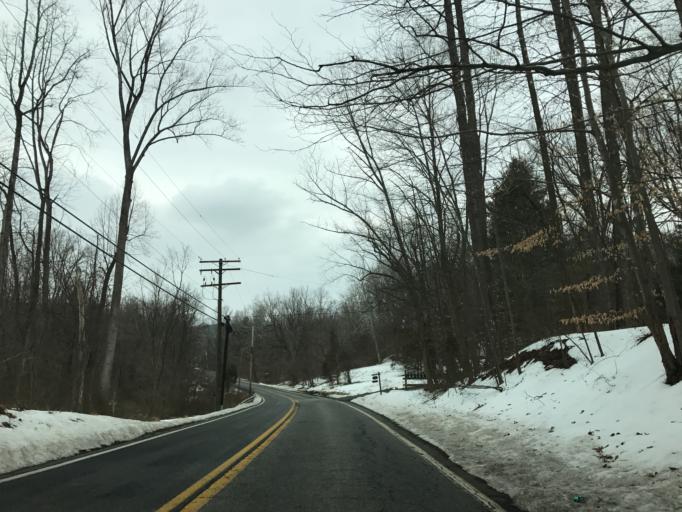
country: US
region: Maryland
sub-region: Harford County
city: Bel Air North
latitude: 39.6140
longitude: -76.4009
